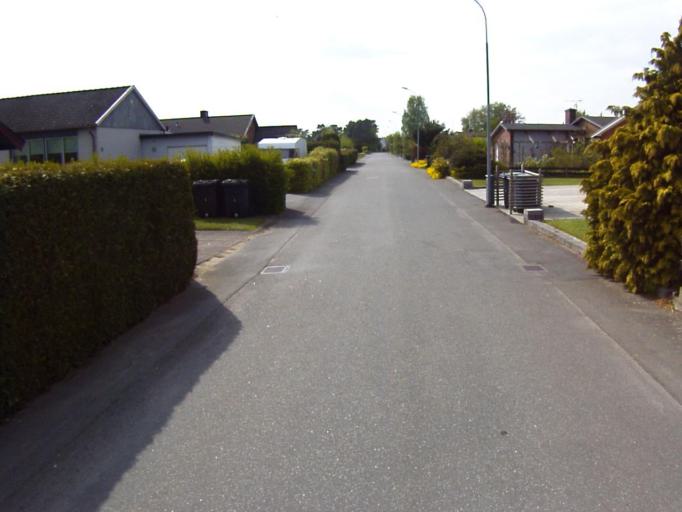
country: SE
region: Skane
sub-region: Kristianstads Kommun
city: Fjalkinge
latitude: 56.0452
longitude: 14.2684
